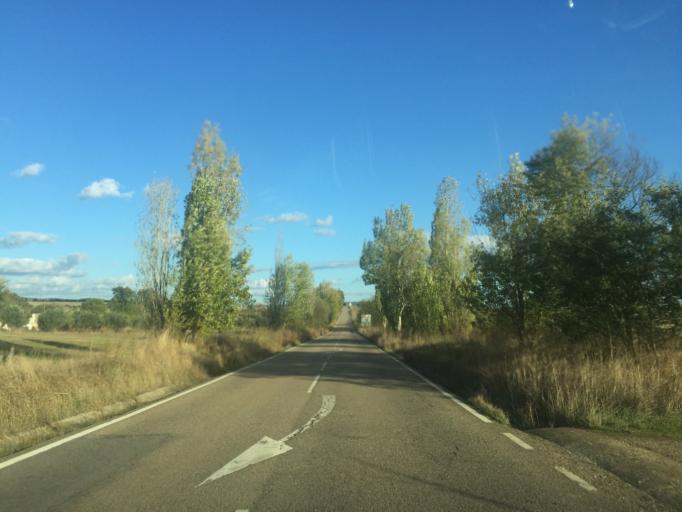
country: PT
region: Portalegre
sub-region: Alter do Chao
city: Alter do Chao
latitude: 39.1997
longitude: -7.7192
